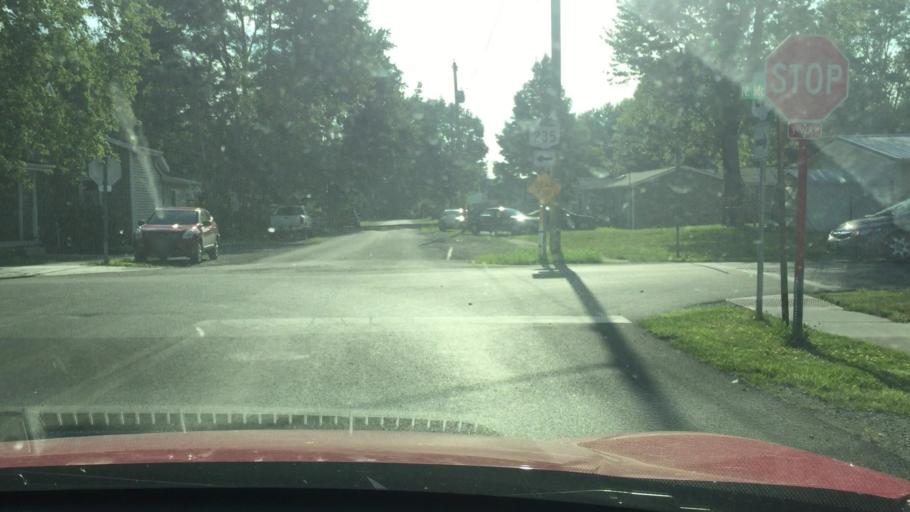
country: US
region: Ohio
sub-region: Hardin County
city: Ada
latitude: 40.7063
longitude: -83.8450
